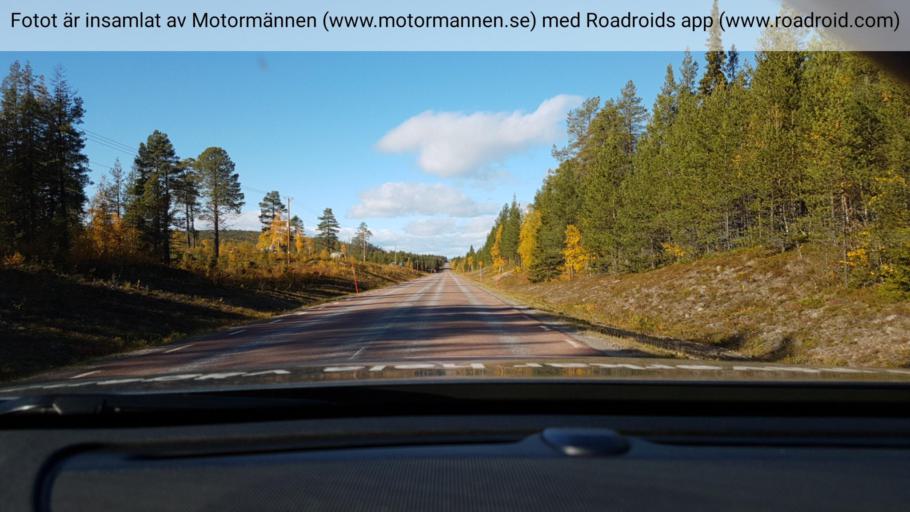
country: SE
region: Norrbotten
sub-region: Arjeplogs Kommun
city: Arjeplog
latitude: 66.0521
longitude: 18.0135
